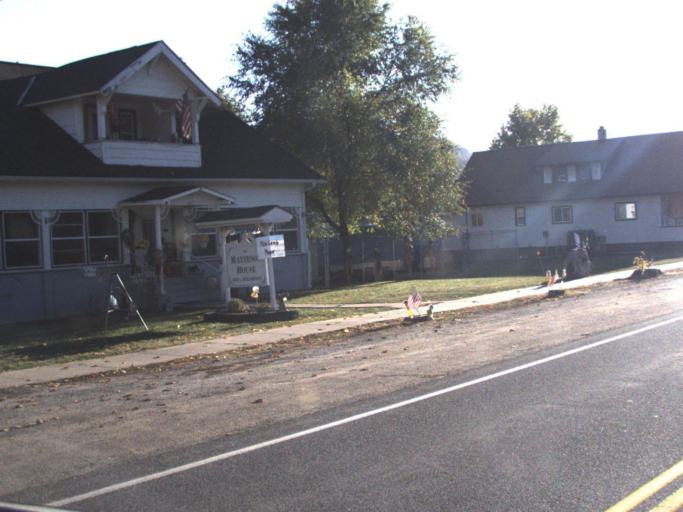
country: CA
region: British Columbia
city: Rossland
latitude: 48.9150
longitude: -117.7849
